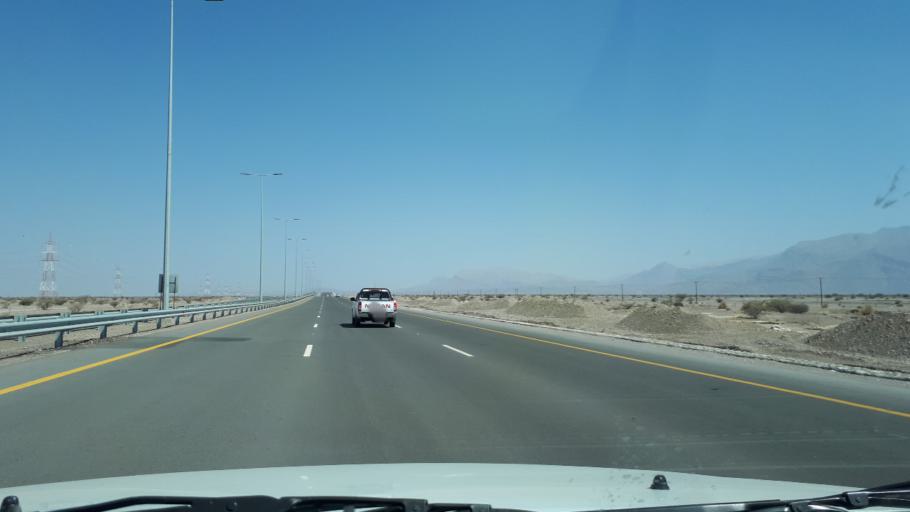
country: OM
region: Ash Sharqiyah
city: Badiyah
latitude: 22.3111
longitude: 59.1407
